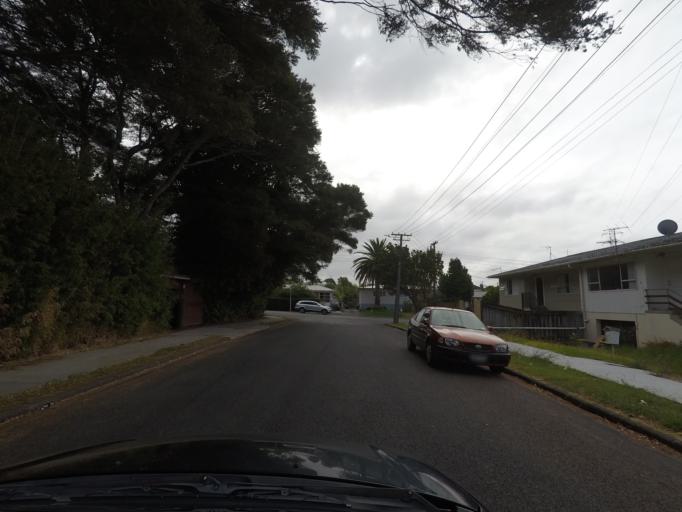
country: NZ
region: Auckland
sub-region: Auckland
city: Rosebank
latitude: -36.8962
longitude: 174.6692
